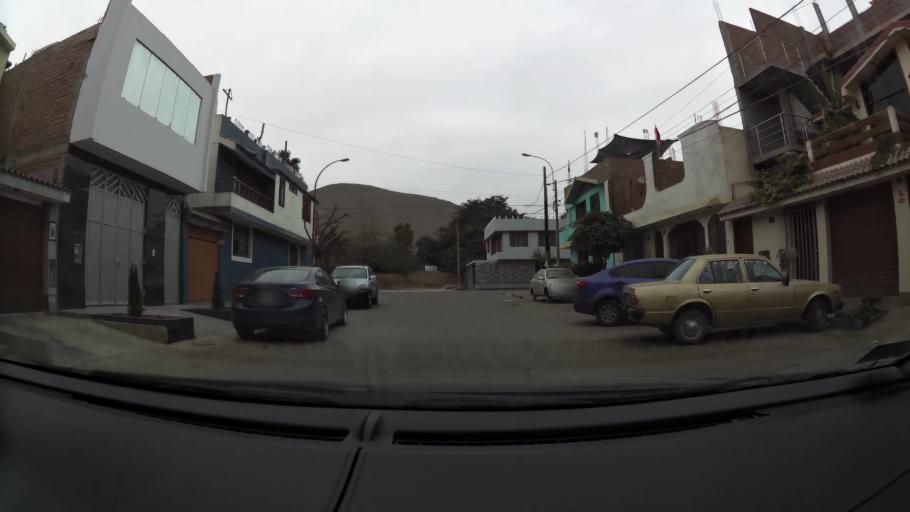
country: PE
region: Lima
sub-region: Lima
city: Independencia
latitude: -11.9409
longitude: -77.0851
